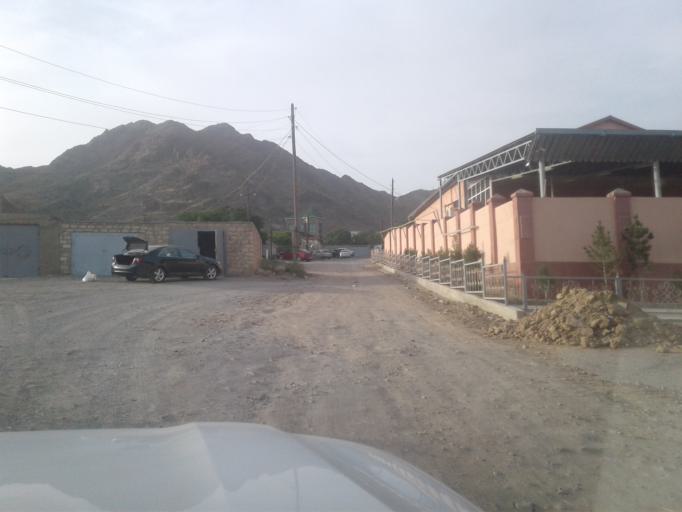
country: TM
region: Balkan
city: Turkmenbasy
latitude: 40.0061
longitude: 52.9651
